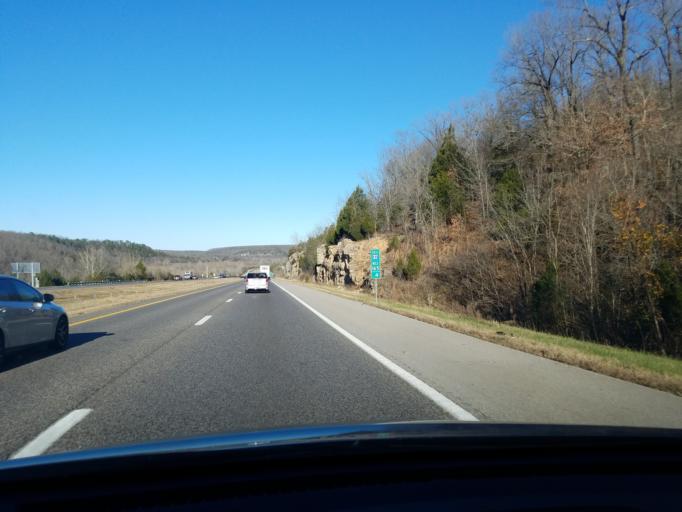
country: US
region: Missouri
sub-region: Pulaski County
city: Saint Robert
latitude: 37.8492
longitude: -92.0804
